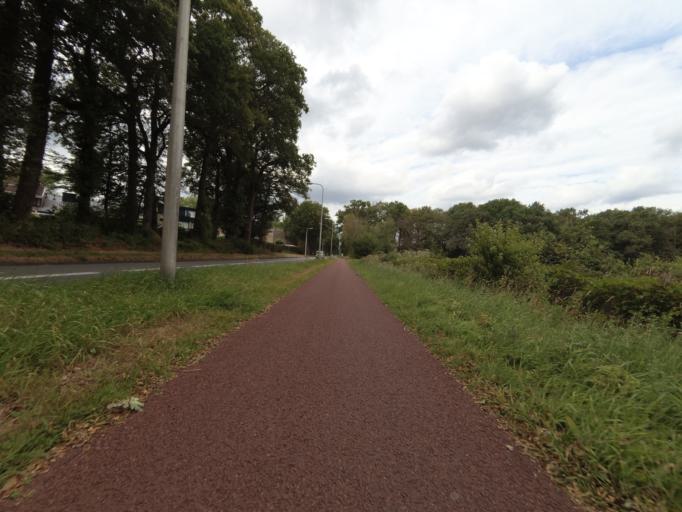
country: NL
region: Overijssel
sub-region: Gemeente Enschede
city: Enschede
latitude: 52.2296
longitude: 6.9258
